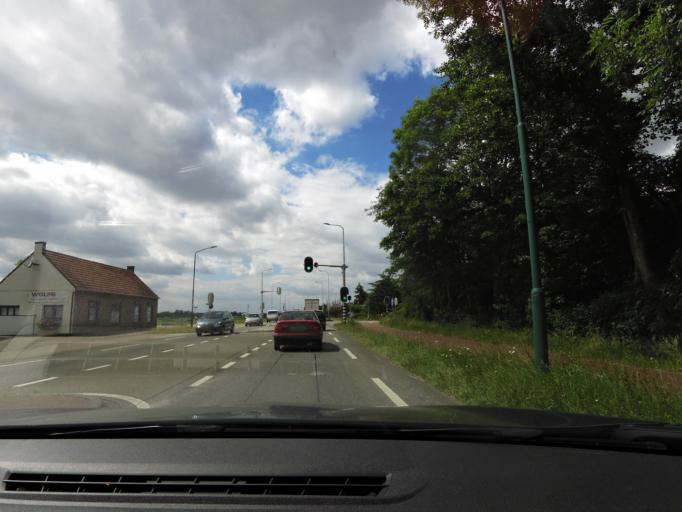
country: NL
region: North Brabant
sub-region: Gemeente Dongen
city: Dongen
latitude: 51.6310
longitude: 4.9118
